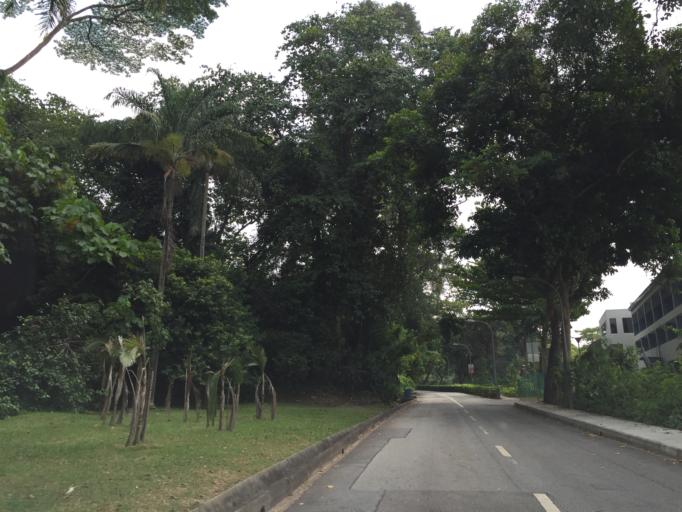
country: SG
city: Singapore
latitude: 1.3240
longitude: 103.8345
